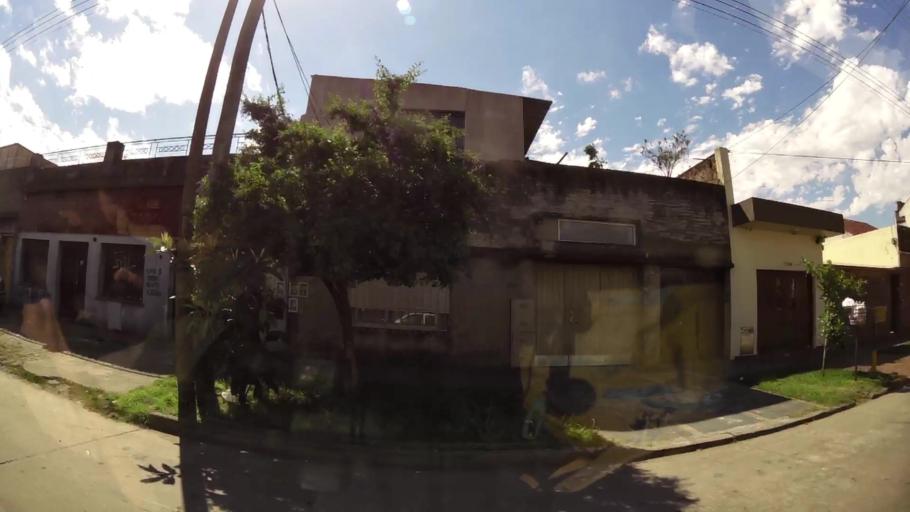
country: AR
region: Buenos Aires
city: San Justo
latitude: -34.6561
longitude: -58.5298
